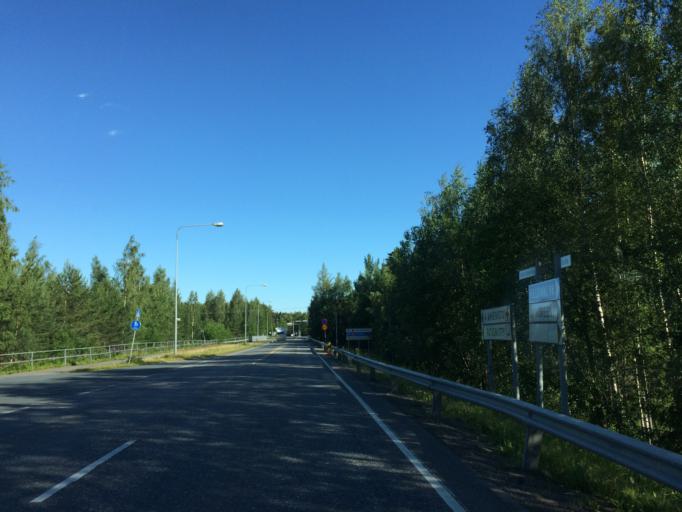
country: FI
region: Haeme
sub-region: Haemeenlinna
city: Haemeenlinna
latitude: 60.9632
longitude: 24.4507
